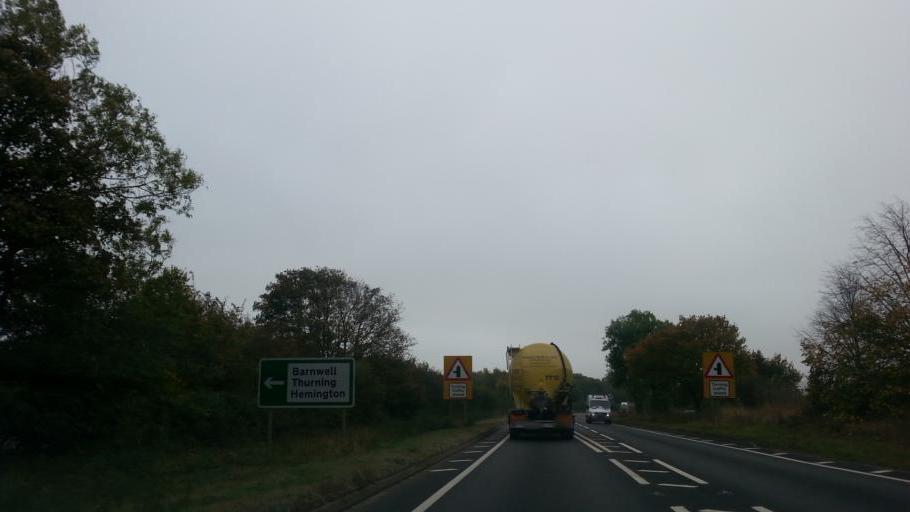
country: GB
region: England
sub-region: Northamptonshire
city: Oundle
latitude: 52.4546
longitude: -0.4625
